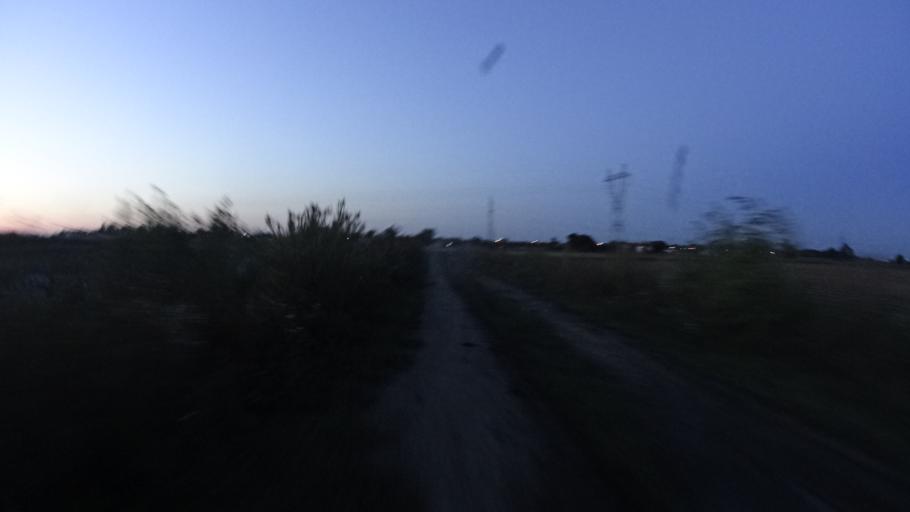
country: PL
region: Masovian Voivodeship
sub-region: Powiat warszawski zachodni
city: Ozarow Mazowiecki
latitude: 52.2260
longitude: 20.7914
